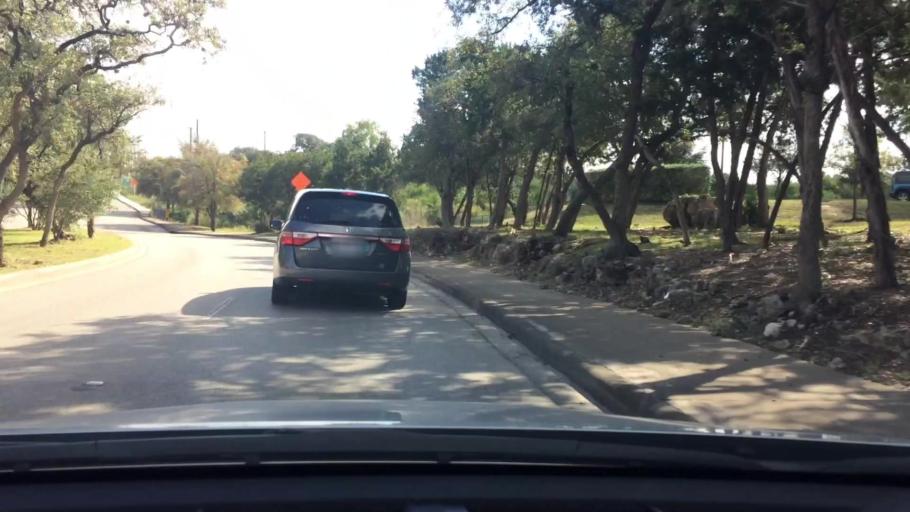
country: US
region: Texas
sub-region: Bexar County
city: Shavano Park
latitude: 29.5787
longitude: -98.5657
